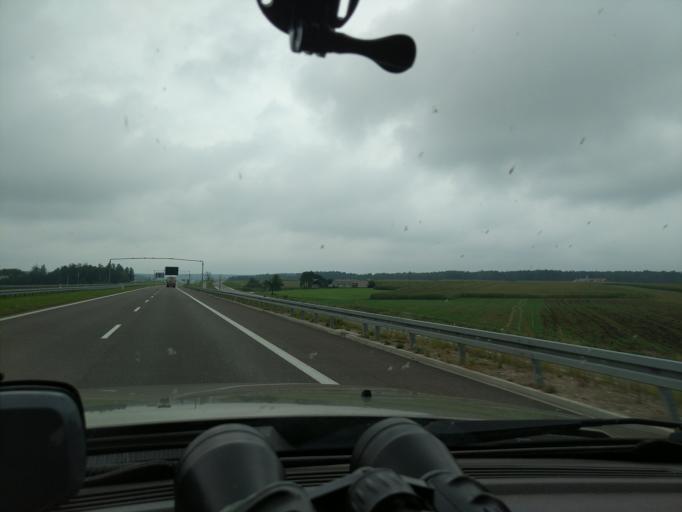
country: PL
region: Podlasie
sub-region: Powiat zambrowski
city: Rutki-Kossaki
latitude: 53.0472
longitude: 22.3728
